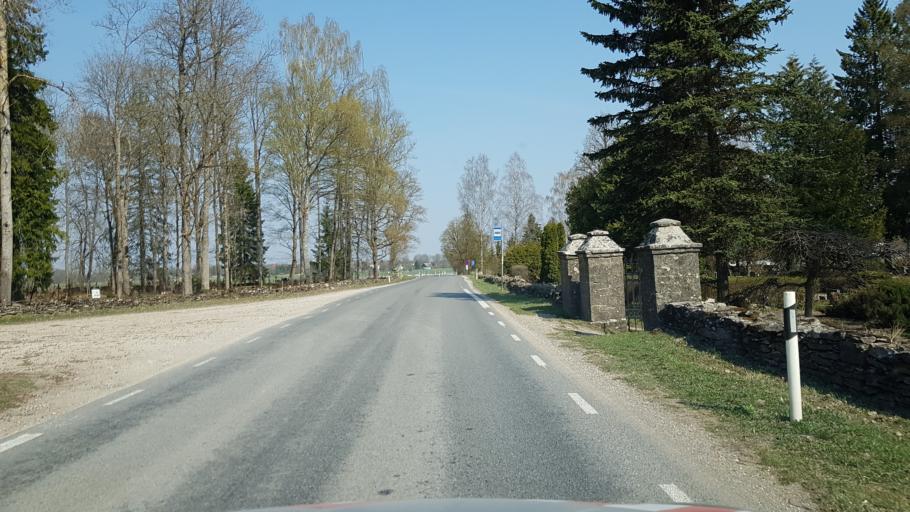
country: EE
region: Raplamaa
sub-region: Kehtna vald
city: Kehtna
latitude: 59.0535
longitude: 24.9504
